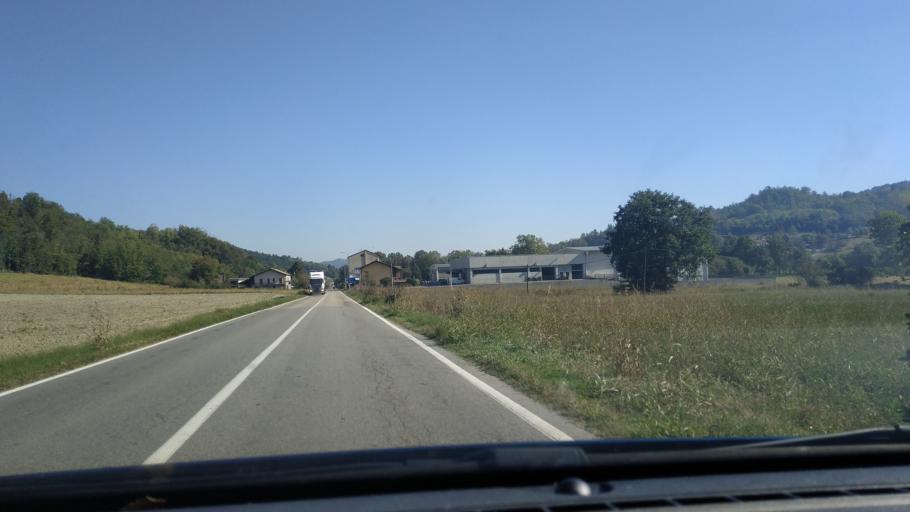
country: IT
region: Piedmont
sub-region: Provincia di Alessandria
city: Cerrina
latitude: 45.1019
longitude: 8.1951
